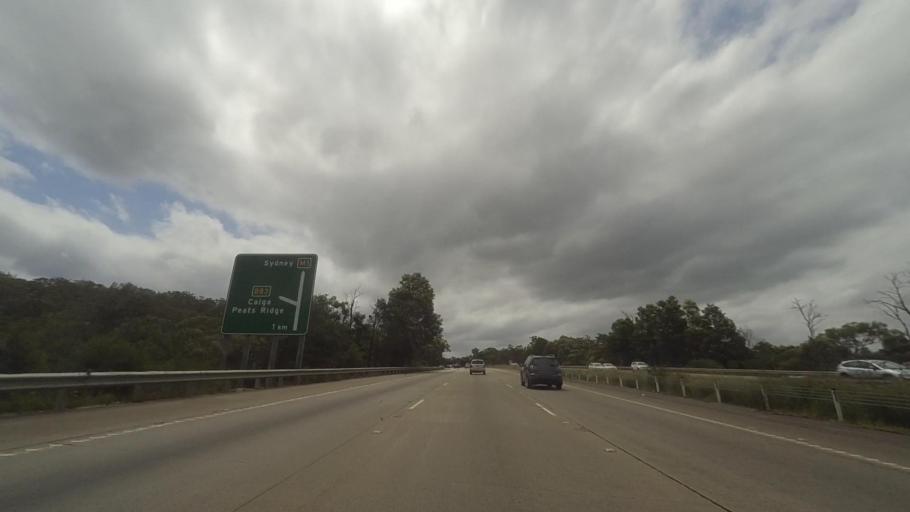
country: AU
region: New South Wales
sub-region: Gosford Shire
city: Point Clare
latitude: -33.4287
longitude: 151.2401
